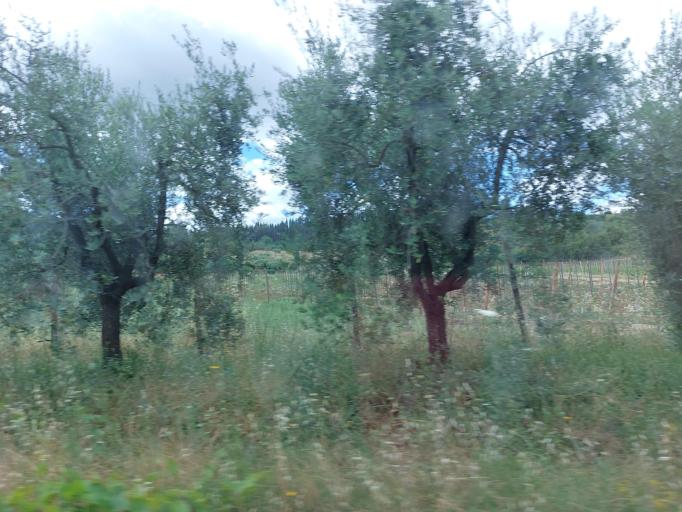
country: IT
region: Tuscany
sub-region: Province of Florence
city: Panzano in Chianti
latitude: 43.5453
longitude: 11.3266
